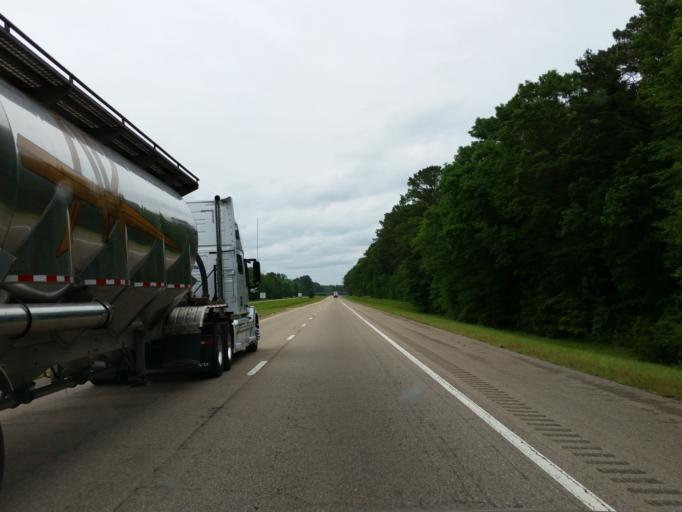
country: US
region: Mississippi
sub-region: Clarke County
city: Stonewall
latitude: 32.0283
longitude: -88.9221
